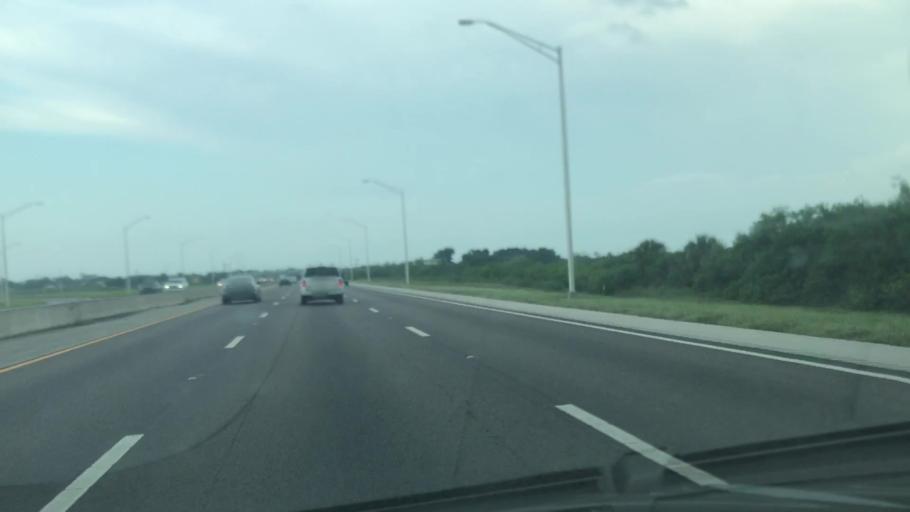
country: US
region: Florida
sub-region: Brevard County
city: Rockledge
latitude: 28.2959
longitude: -80.7489
